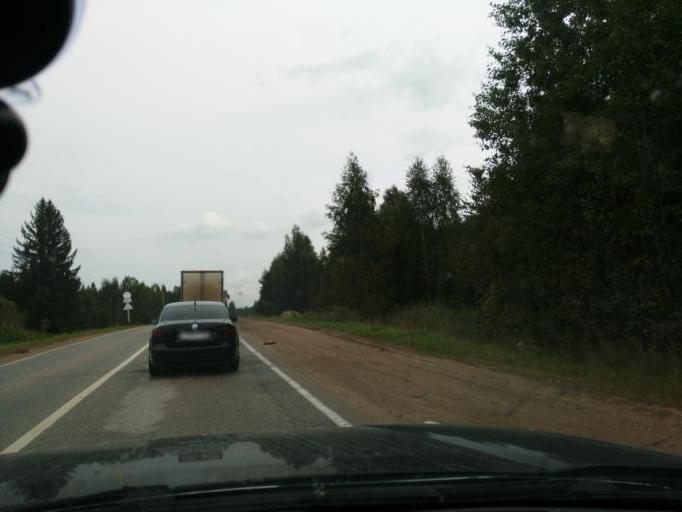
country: RU
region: Bashkortostan
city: Verkhniye Tatyshly
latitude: 56.4960
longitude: 55.8276
